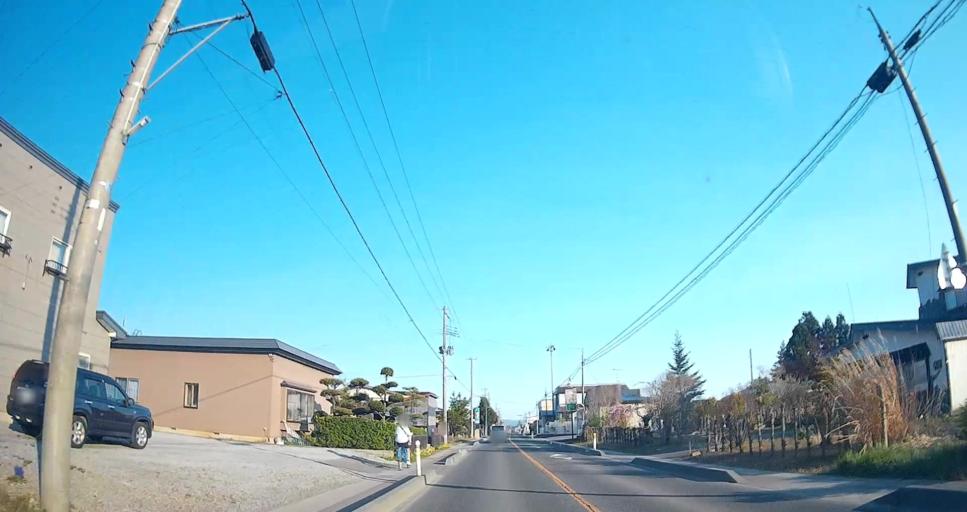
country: JP
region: Aomori
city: Mutsu
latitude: 41.2710
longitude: 141.2180
